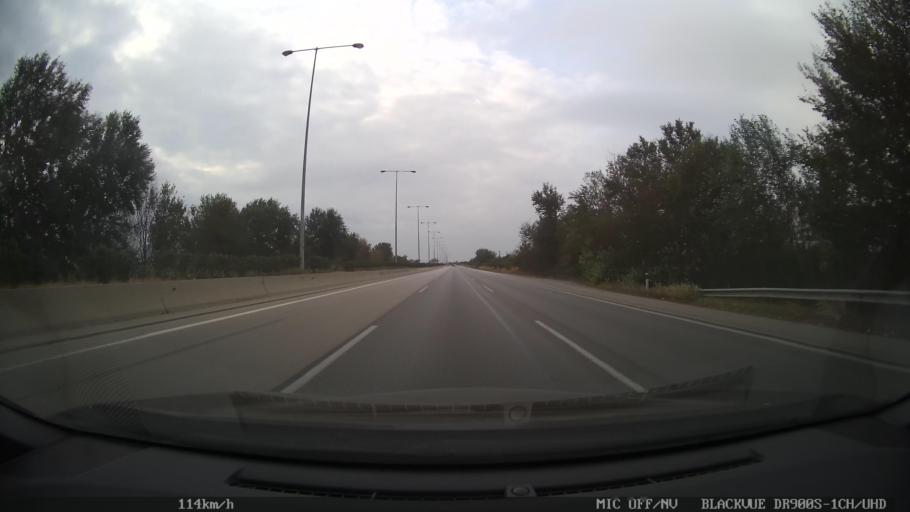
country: GR
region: Central Macedonia
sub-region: Nomos Thessalonikis
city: Nea Magnisia
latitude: 40.6828
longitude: 22.8325
